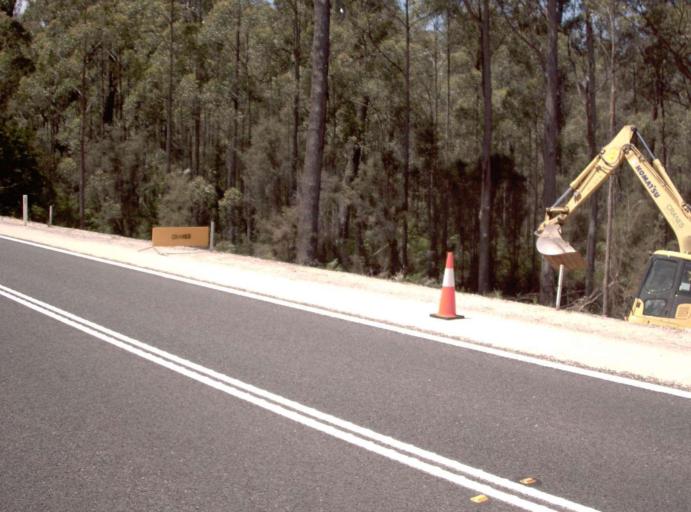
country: AU
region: New South Wales
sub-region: Bombala
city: Bombala
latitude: -37.6255
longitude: 148.8894
